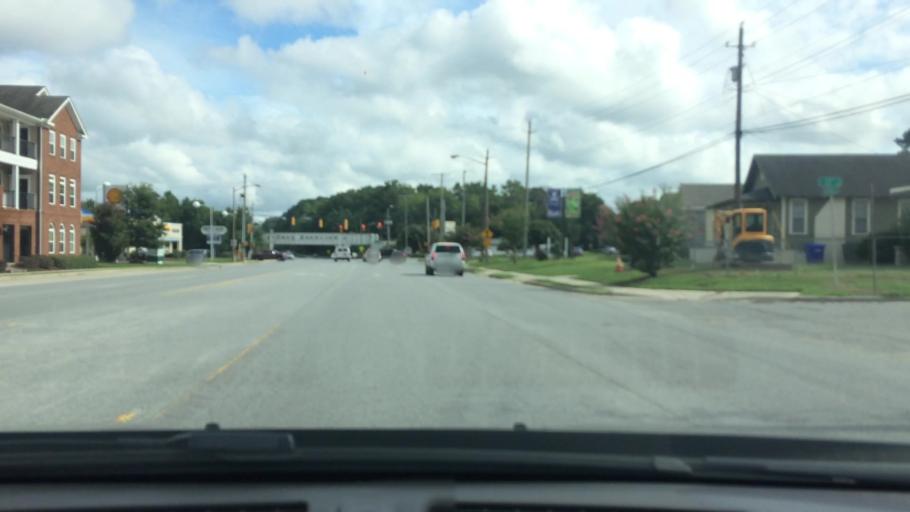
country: US
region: North Carolina
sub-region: Pitt County
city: Greenville
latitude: 35.6023
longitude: -77.3710
